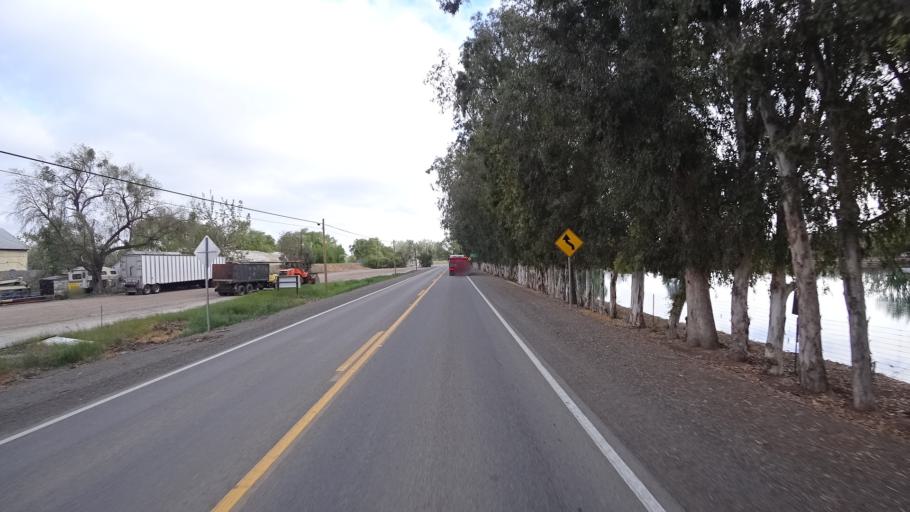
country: US
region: California
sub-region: Glenn County
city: Willows
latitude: 39.4607
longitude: -121.9926
